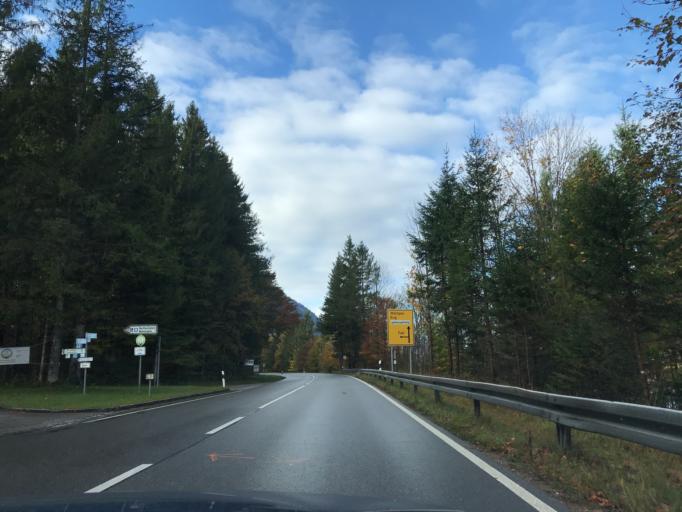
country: DE
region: Bavaria
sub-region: Upper Bavaria
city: Jachenau
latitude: 47.5721
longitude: 11.5331
